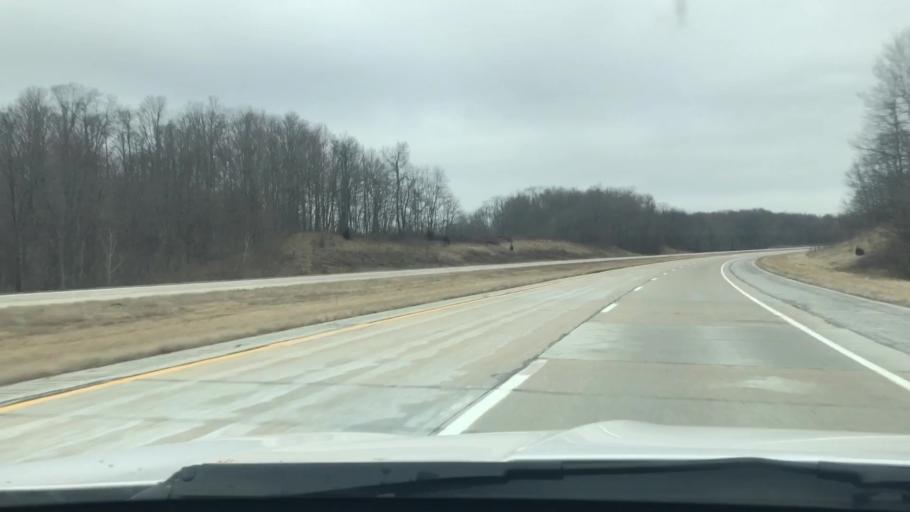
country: US
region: Indiana
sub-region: Miami County
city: Peru
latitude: 40.7669
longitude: -86.1667
